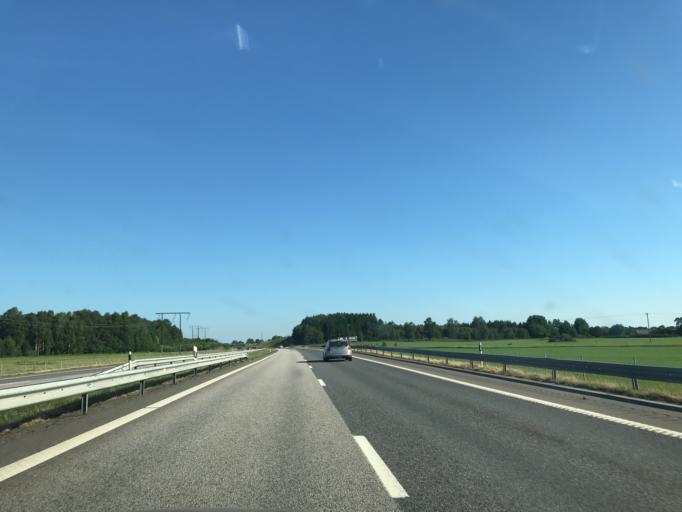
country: SE
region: Halland
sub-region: Varbergs Kommun
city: Tvaaker
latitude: 57.0798
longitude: 12.3498
